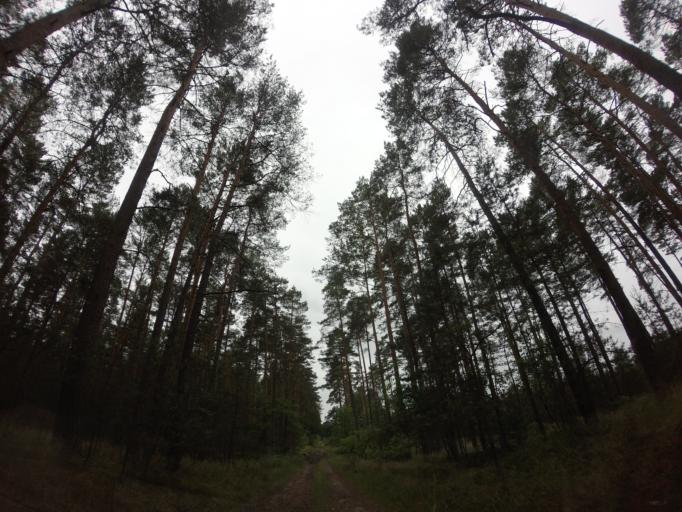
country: PL
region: West Pomeranian Voivodeship
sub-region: Powiat choszczenski
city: Drawno
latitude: 53.1362
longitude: 15.7723
